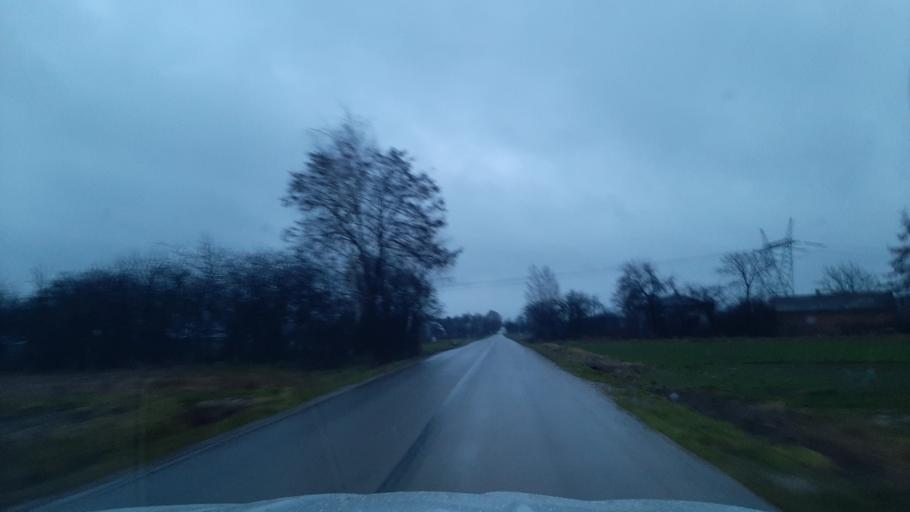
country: PL
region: Lublin Voivodeship
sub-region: Powiat lubelski
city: Jastkow
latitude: 51.3562
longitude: 22.4203
